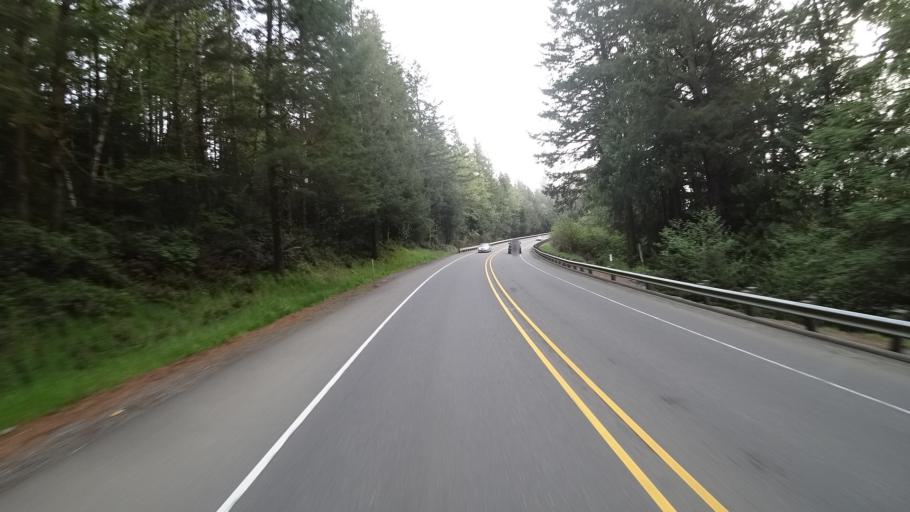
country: US
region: Oregon
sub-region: Coos County
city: Barview
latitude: 43.2538
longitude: -124.2855
